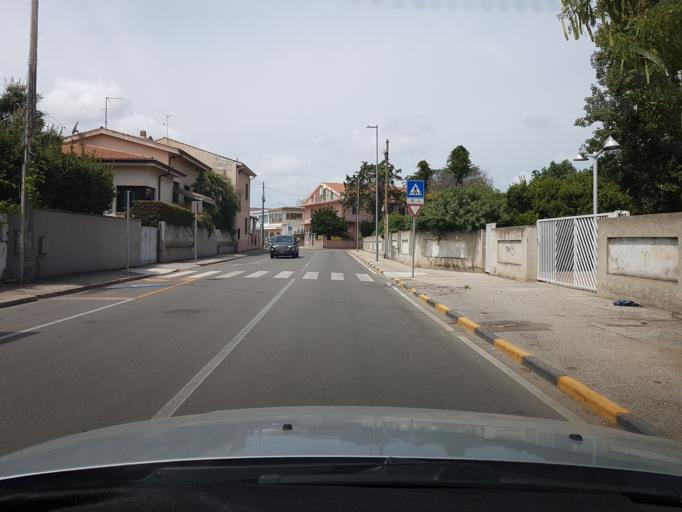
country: IT
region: Sardinia
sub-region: Provincia di Oristano
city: Oristano
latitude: 39.9114
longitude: 8.5912
